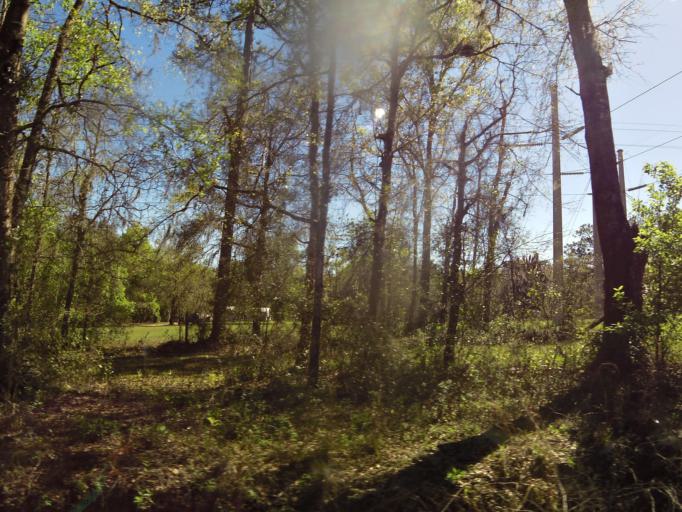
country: US
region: Florida
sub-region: Clay County
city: Keystone Heights
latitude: 29.8165
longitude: -82.0555
